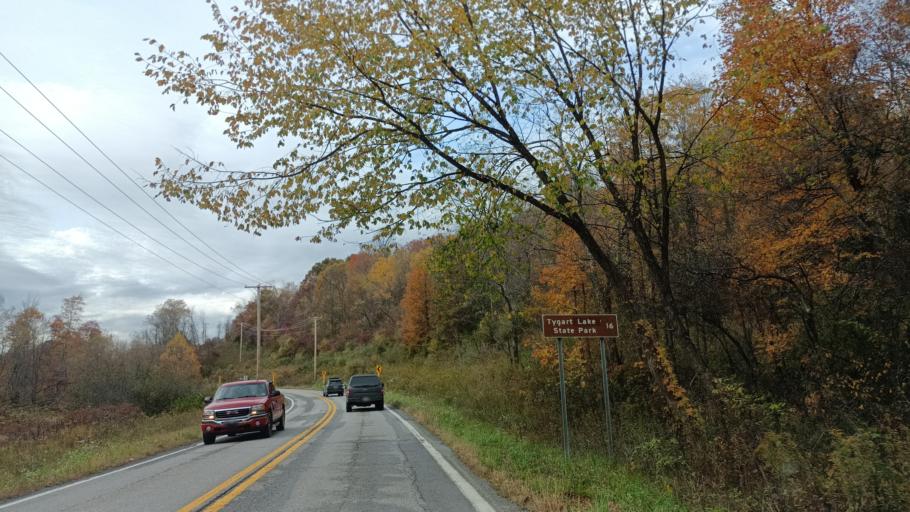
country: US
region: West Virginia
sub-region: Taylor County
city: Grafton
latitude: 39.3359
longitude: -79.8513
